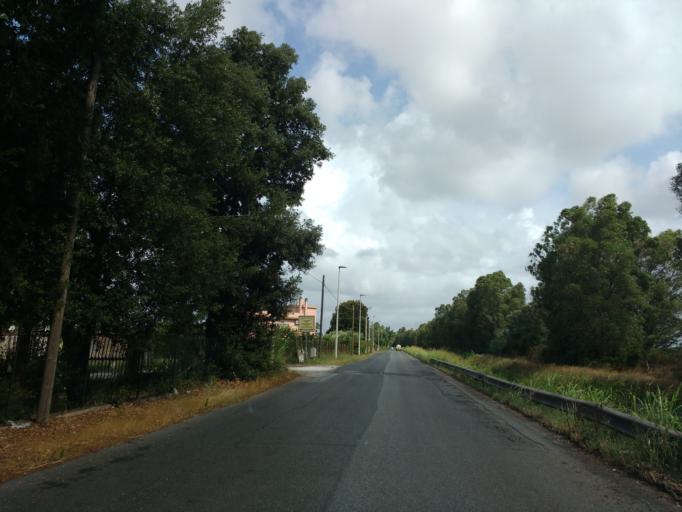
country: IT
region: Latium
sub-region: Citta metropolitana di Roma Capitale
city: Acilia-Castel Fusano-Ostia Antica
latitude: 41.7551
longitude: 12.3300
